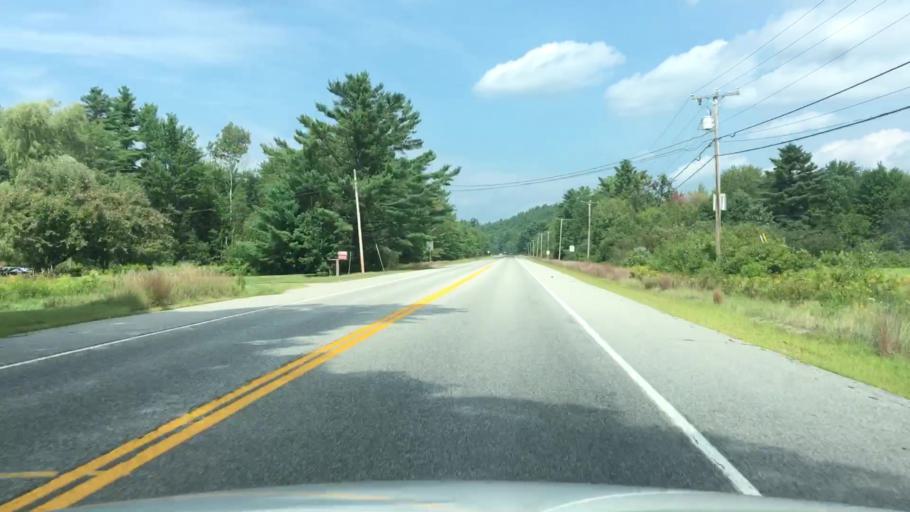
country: US
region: Maine
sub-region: Oxford County
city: Canton
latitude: 44.4466
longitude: -70.3170
